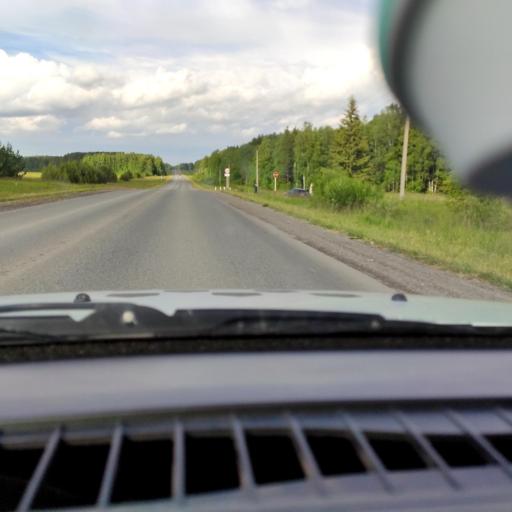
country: RU
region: Perm
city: Orda
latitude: 57.2356
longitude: 56.9768
